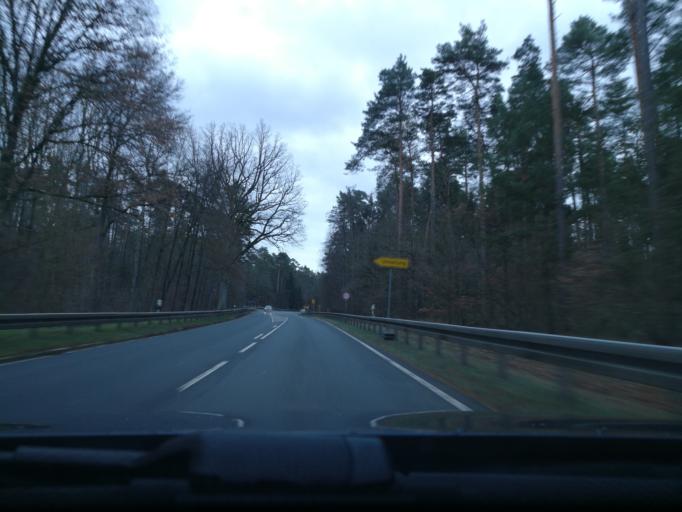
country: DE
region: Bavaria
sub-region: Upper Franconia
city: Dormitz
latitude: 49.5869
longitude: 11.1078
